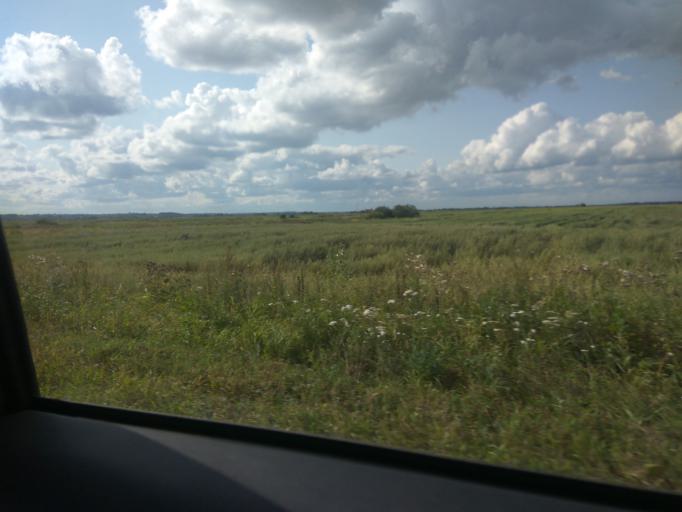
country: RU
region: Moskovskaya
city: Ramenskoye
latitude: 55.5066
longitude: 38.2518
